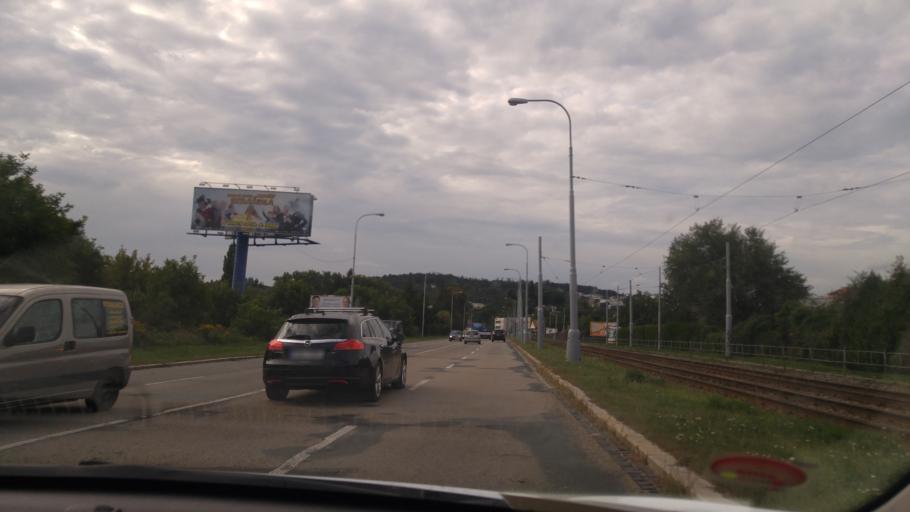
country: CZ
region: South Moravian
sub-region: Mesto Brno
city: Brno
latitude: 49.2151
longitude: 16.5567
